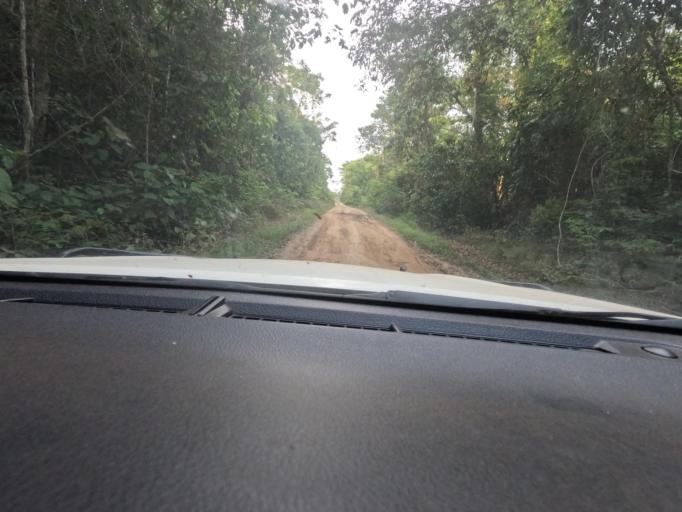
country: BR
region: Rondonia
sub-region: Porto Velho
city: Porto Velho
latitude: -8.6488
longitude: -63.1559
